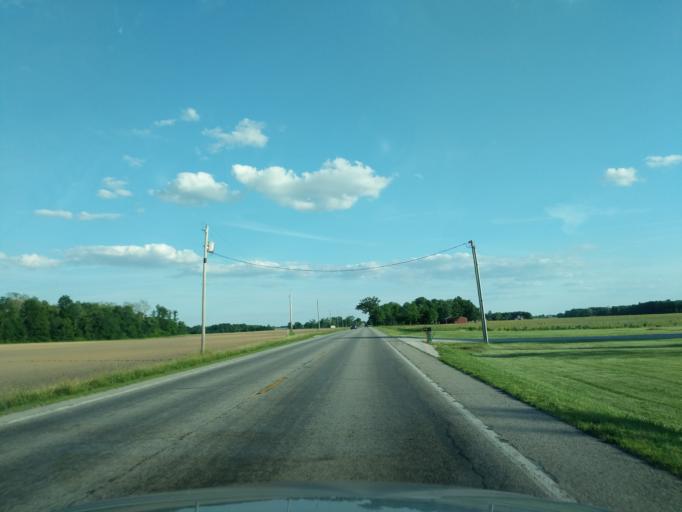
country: US
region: Indiana
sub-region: Huntington County
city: Huntington
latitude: 40.7990
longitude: -85.4605
